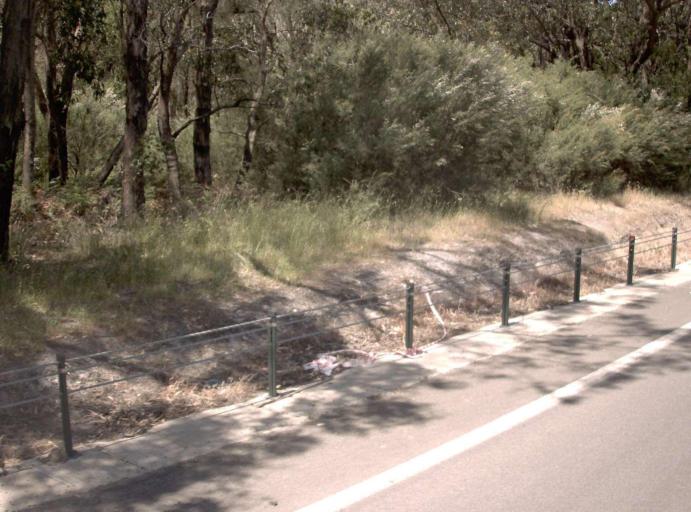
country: AU
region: Victoria
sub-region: Latrobe
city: Moe
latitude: -38.2131
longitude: 146.3241
